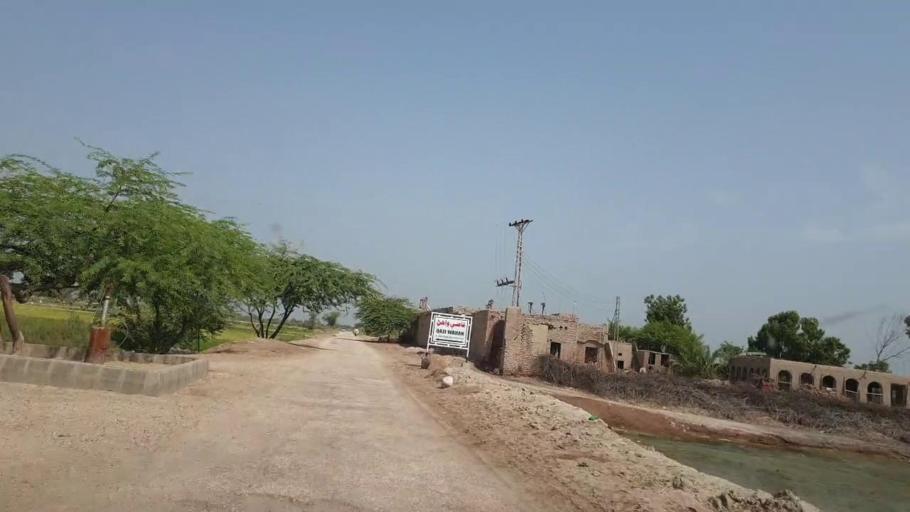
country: PK
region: Sindh
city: Lakhi
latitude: 27.8296
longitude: 68.6852
